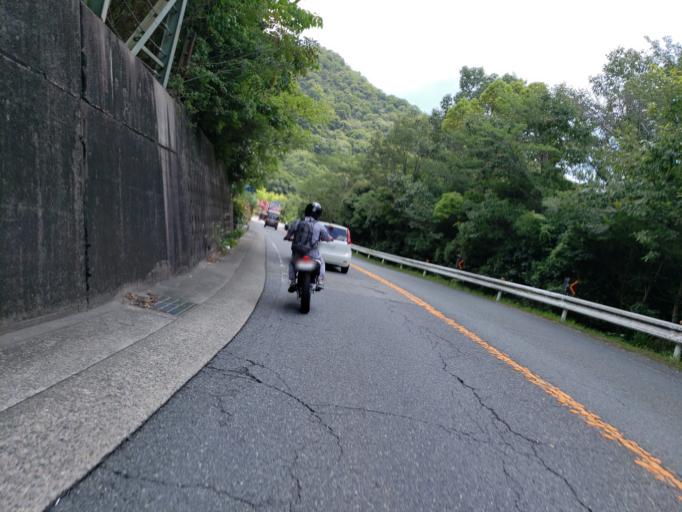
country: JP
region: Hyogo
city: Aioi
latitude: 34.7790
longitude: 134.4353
